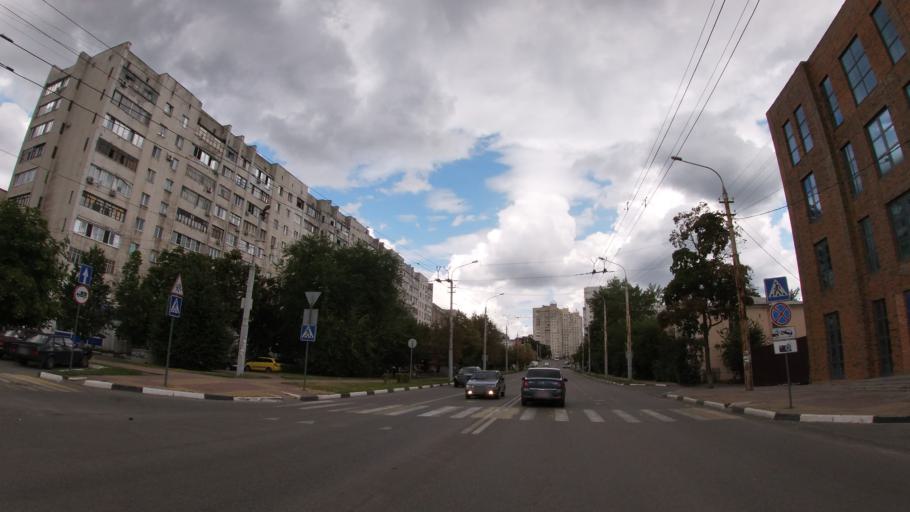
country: RU
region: Belgorod
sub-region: Belgorodskiy Rayon
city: Belgorod
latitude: 50.5963
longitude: 36.6062
